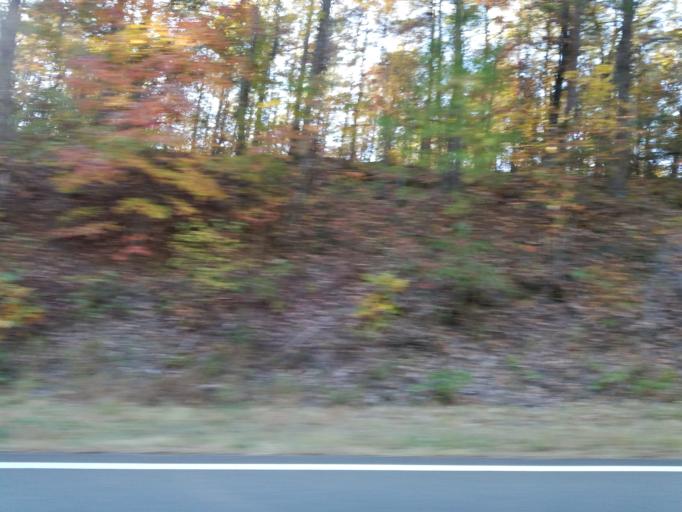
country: US
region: Georgia
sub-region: Pickens County
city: Jasper
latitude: 34.5365
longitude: -84.4785
